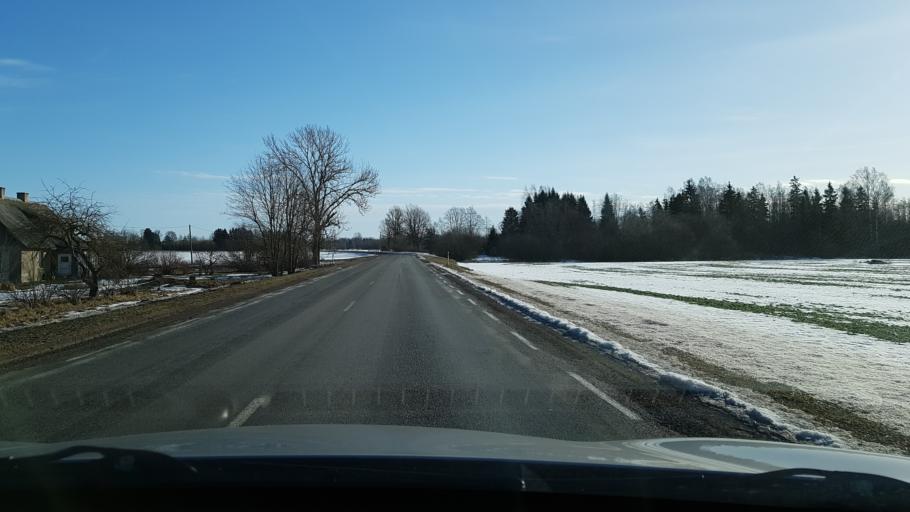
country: EE
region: Viljandimaa
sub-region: Vohma linn
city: Vohma
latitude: 58.6301
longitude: 25.6203
